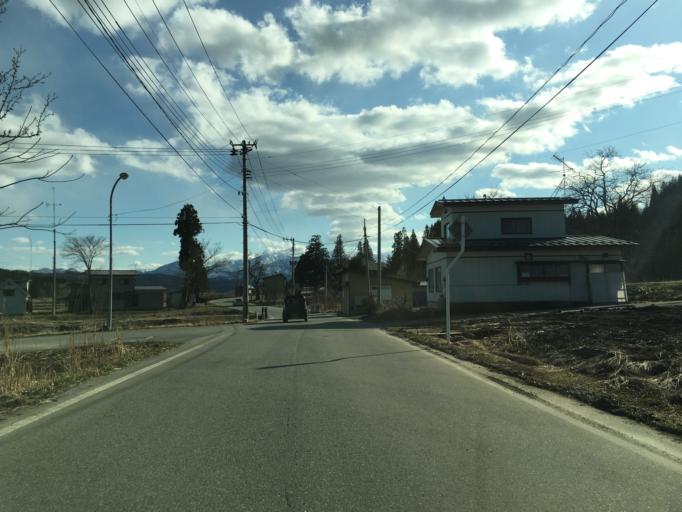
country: JP
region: Yamagata
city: Yonezawa
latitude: 37.9678
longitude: 139.9921
